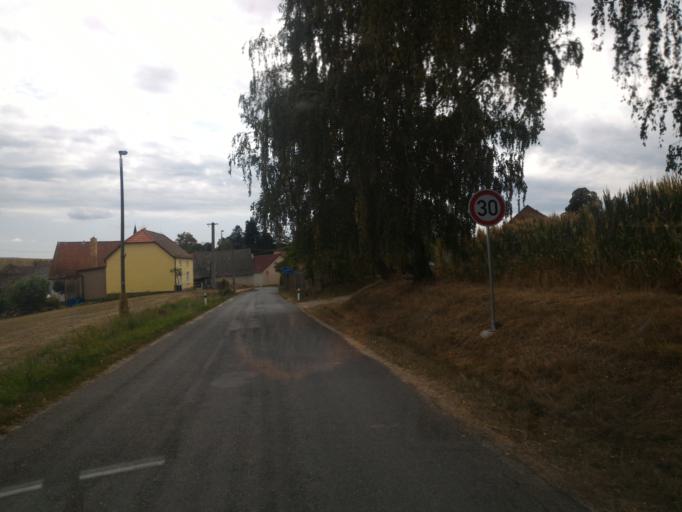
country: CZ
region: Jihocesky
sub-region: Okres Jindrichuv Hradec
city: Dacice
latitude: 49.1096
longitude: 15.4207
